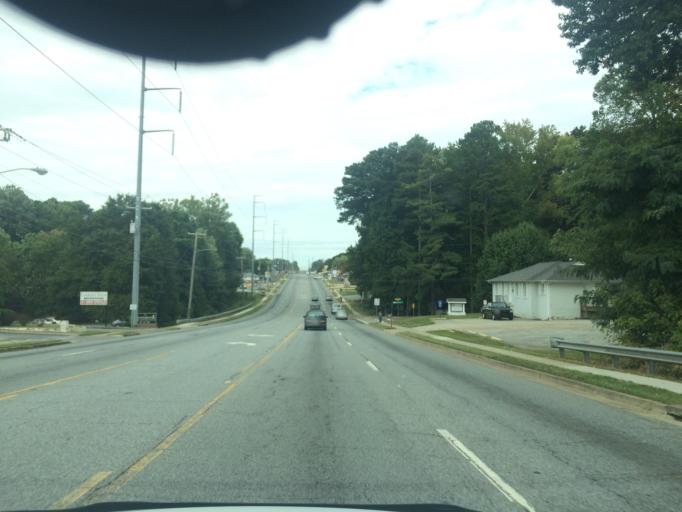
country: US
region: Georgia
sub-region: Cobb County
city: Smyrna
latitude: 33.8944
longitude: -84.5286
